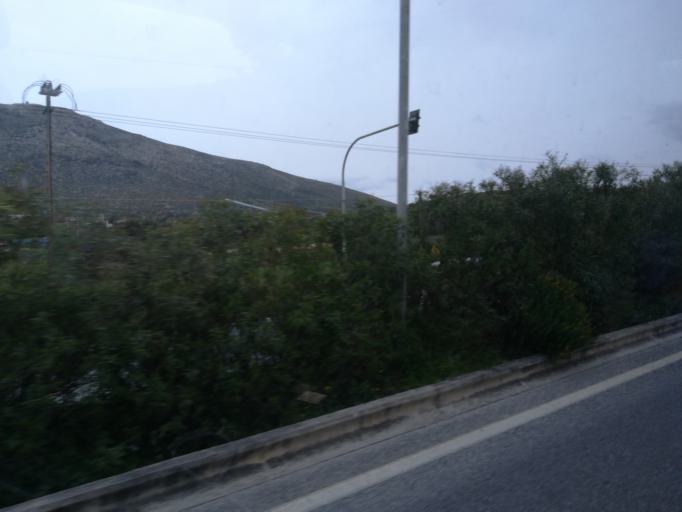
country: GR
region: Attica
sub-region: Nomarchia Anatolikis Attikis
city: Kalyvia Thorikou
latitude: 37.8398
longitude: 23.9427
